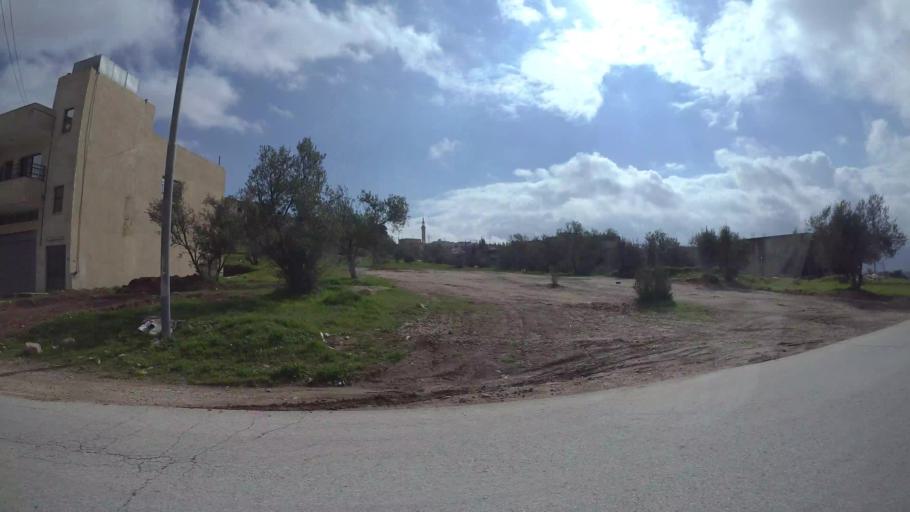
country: JO
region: Amman
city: Al Jubayhah
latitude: 32.0719
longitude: 35.8624
